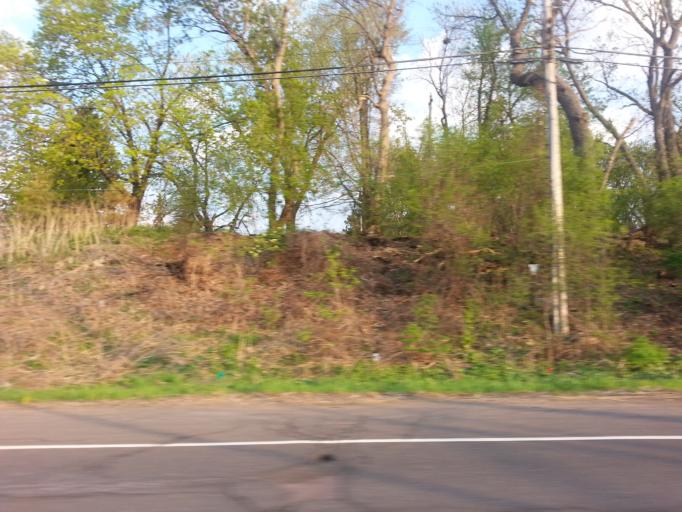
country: US
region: Minnesota
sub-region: Dakota County
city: Mendota Heights
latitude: 44.8990
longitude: -93.1398
